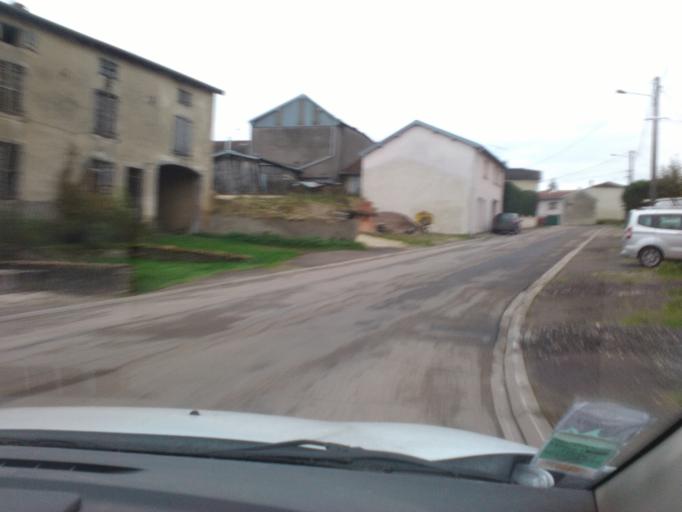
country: FR
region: Lorraine
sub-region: Departement des Vosges
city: Darnieulles
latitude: 48.2542
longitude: 6.2820
